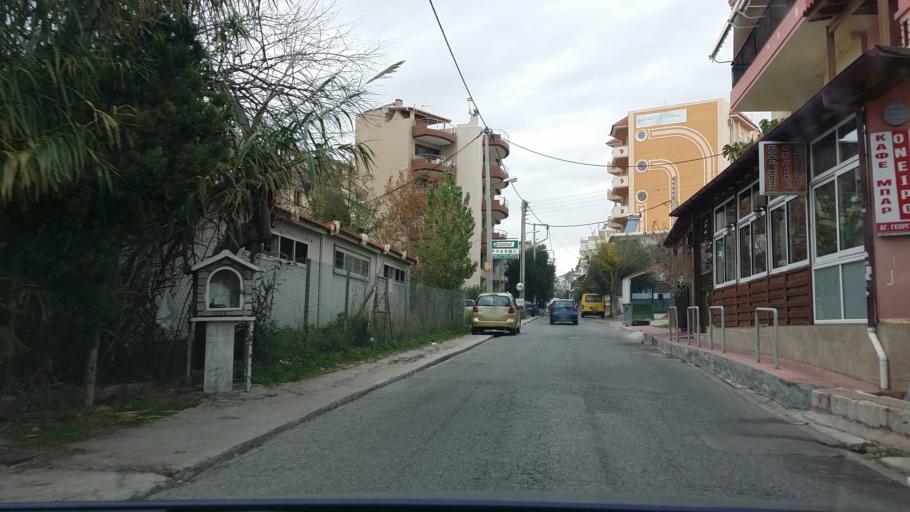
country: GR
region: Attica
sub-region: Nomarchia Athinas
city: Peristeri
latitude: 38.0259
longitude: 23.6906
